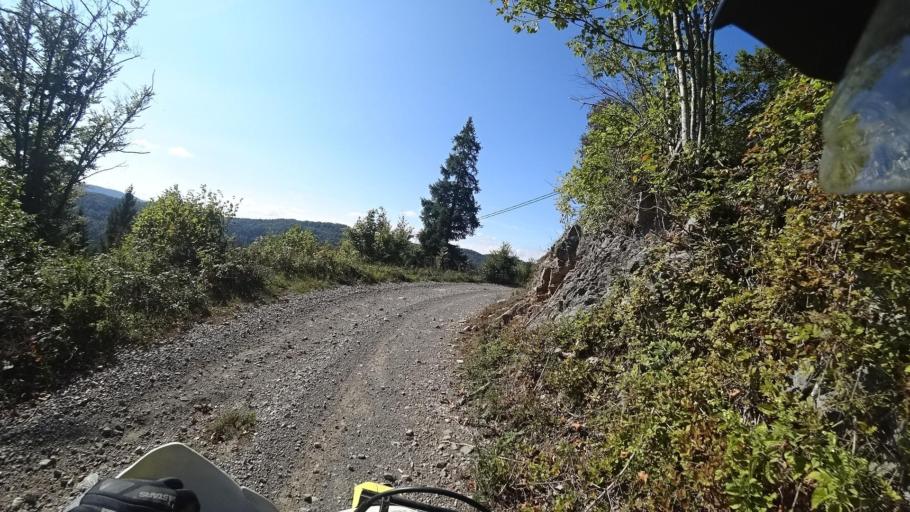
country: HR
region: Karlovacka
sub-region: Grad Ogulin
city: Ogulin
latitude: 45.2505
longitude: 15.1412
